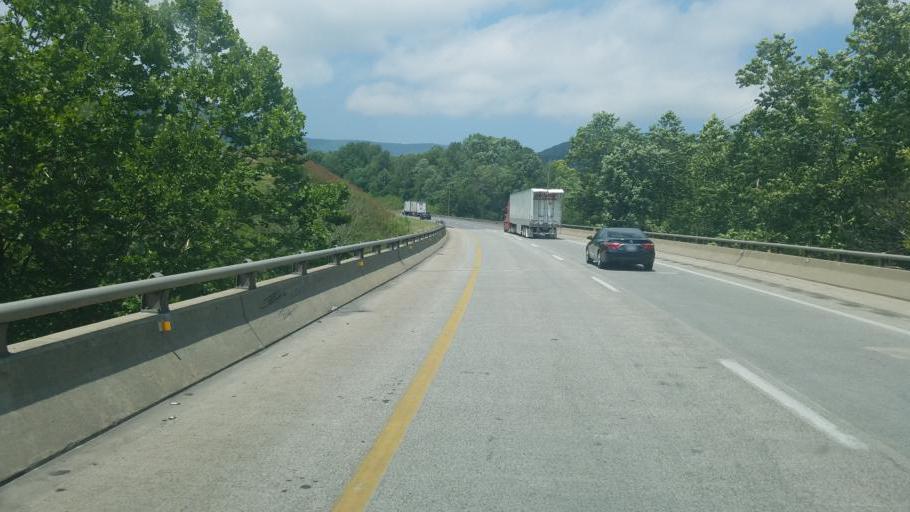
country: US
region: West Virginia
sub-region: Mercer County
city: Bluefield
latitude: 37.2358
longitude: -81.0966
